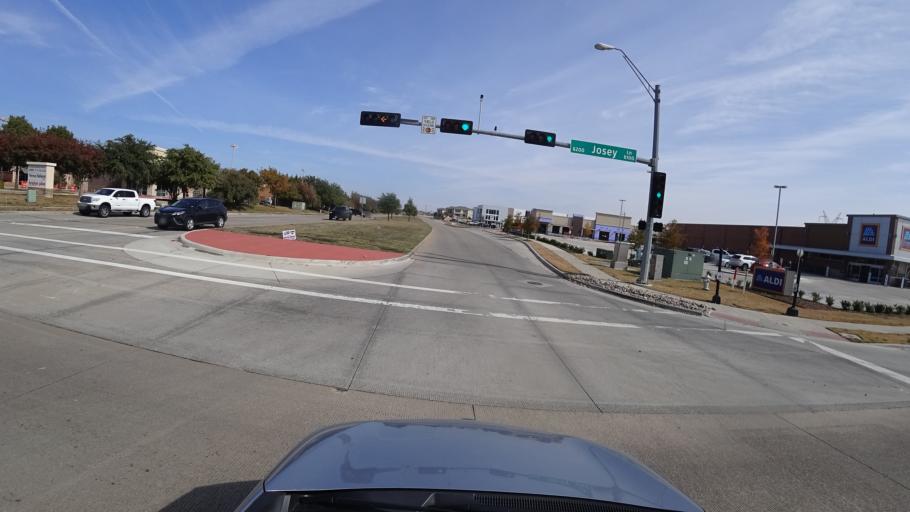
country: US
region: Texas
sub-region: Denton County
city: The Colony
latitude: 33.0619
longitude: -96.8864
